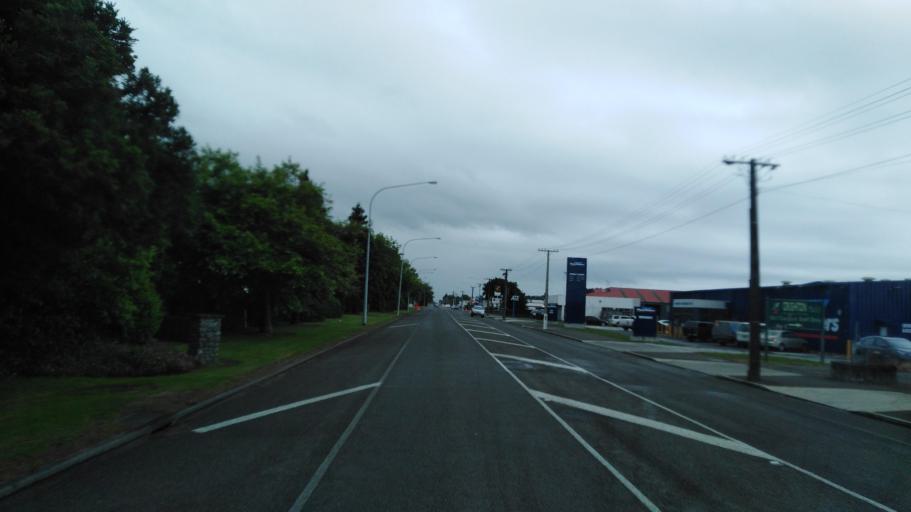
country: NZ
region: Manawatu-Wanganui
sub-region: Horowhenua District
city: Levin
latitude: -40.6347
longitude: 175.2742
